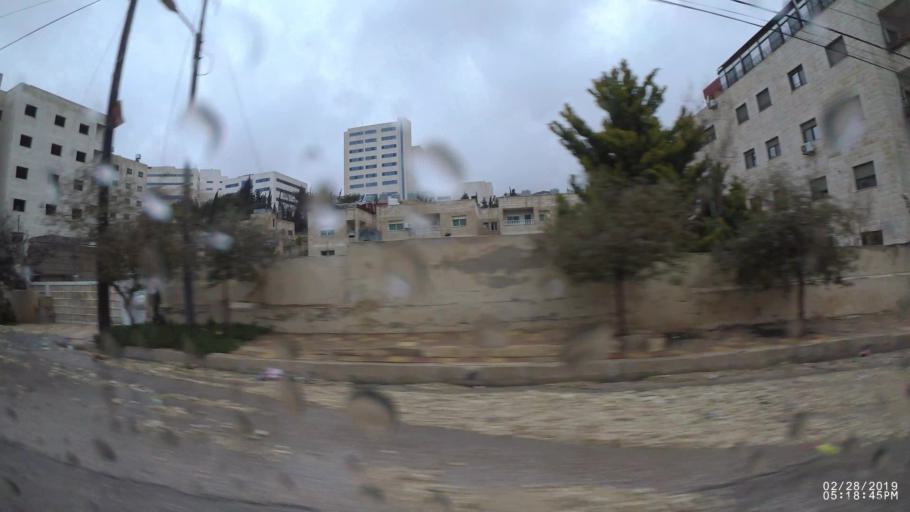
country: JO
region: Amman
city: Amman
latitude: 32.0003
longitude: 35.9216
